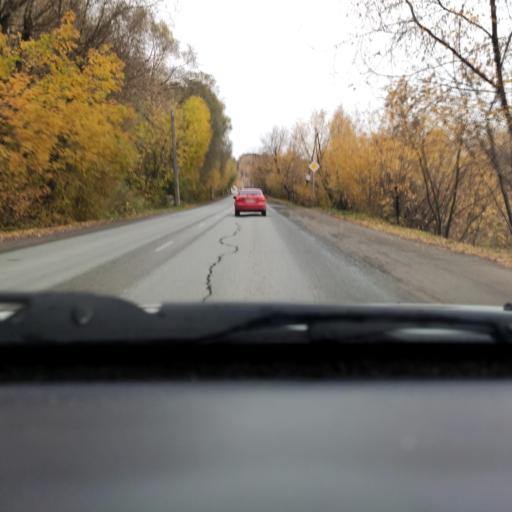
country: RU
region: Perm
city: Perm
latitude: 58.0617
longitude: 56.3394
